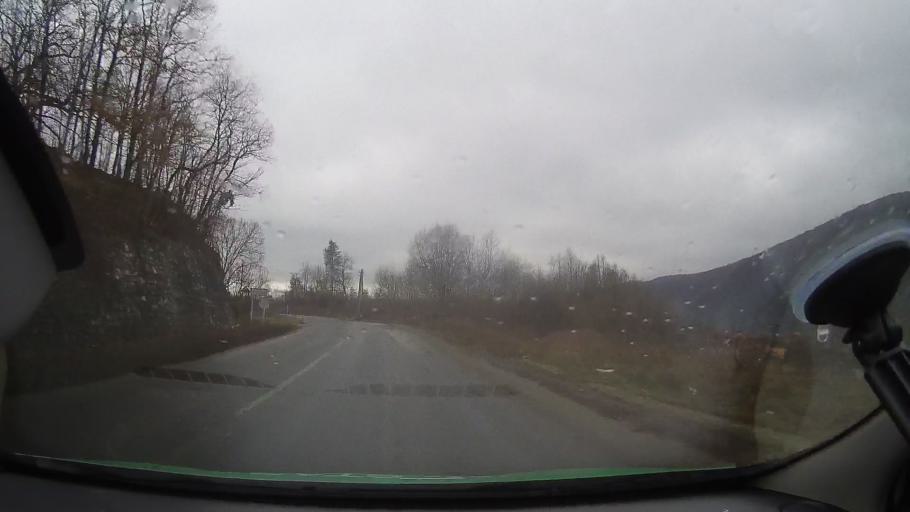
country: RO
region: Arad
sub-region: Comuna Halmagiu
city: Halmagiu
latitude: 46.2355
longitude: 22.5576
